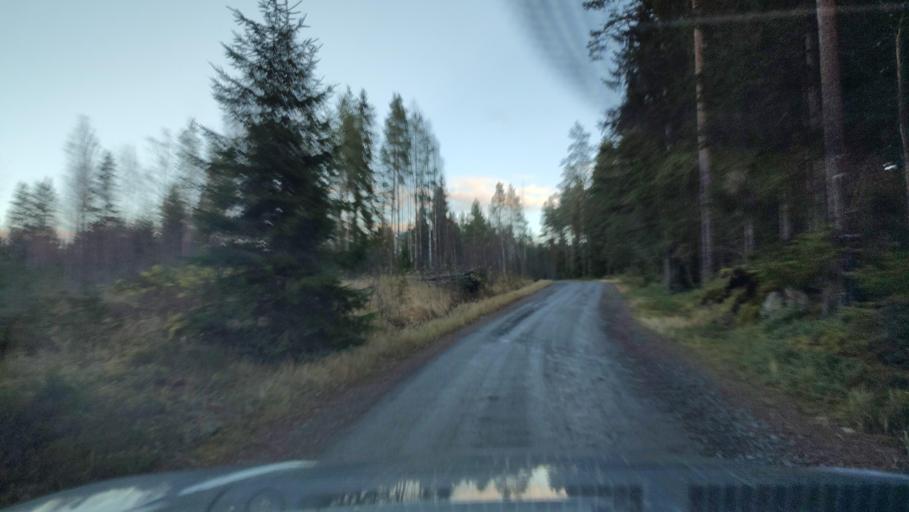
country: FI
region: Southern Ostrobothnia
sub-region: Suupohja
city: Karijoki
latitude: 62.2875
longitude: 21.6256
